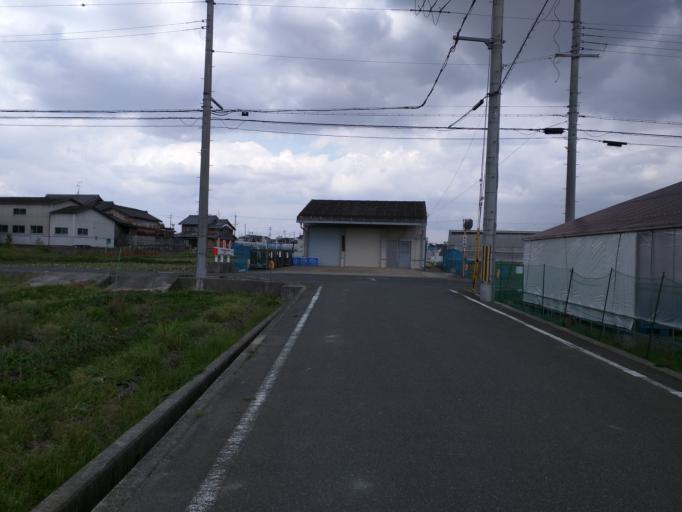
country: JP
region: Kyoto
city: Tanabe
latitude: 34.7742
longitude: 135.7935
